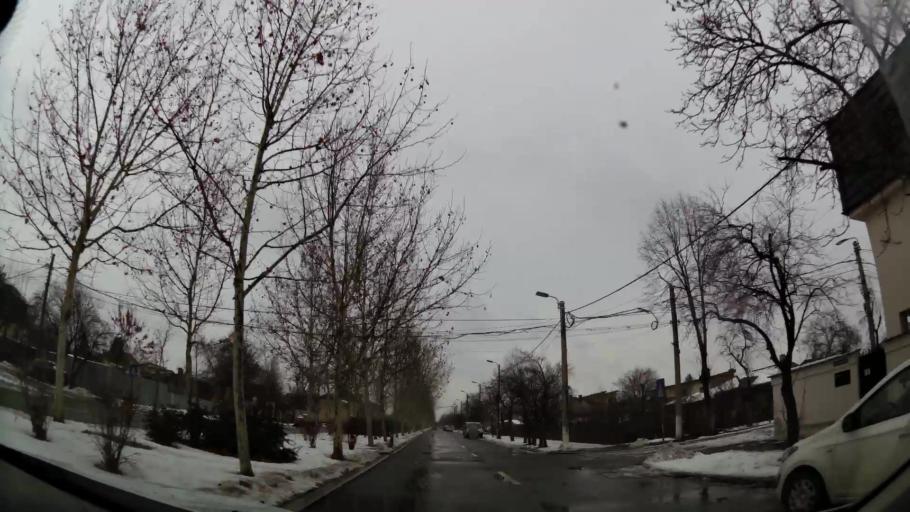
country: RO
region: Ilfov
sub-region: Comuna Chiajna
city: Rosu
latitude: 44.4894
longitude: 26.0213
